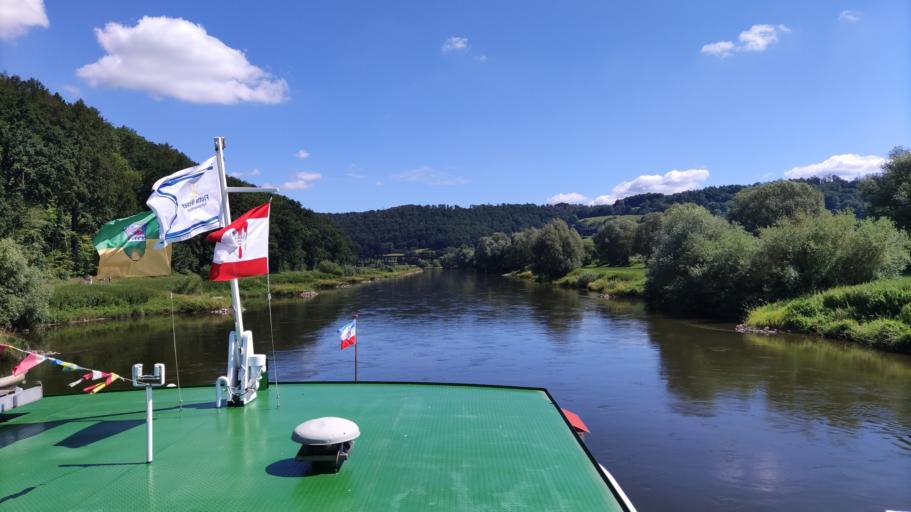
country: DE
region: North Rhine-Westphalia
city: Beverungen
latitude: 51.6930
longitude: 9.3911
